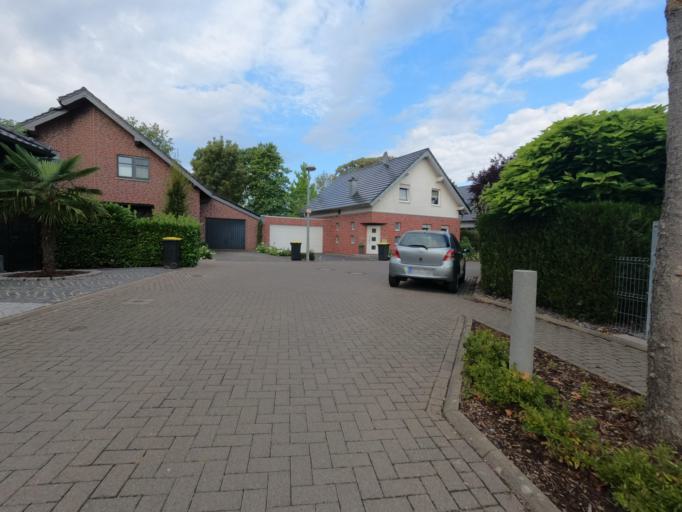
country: DE
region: North Rhine-Westphalia
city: Wegberg
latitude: 51.1037
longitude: 6.2757
